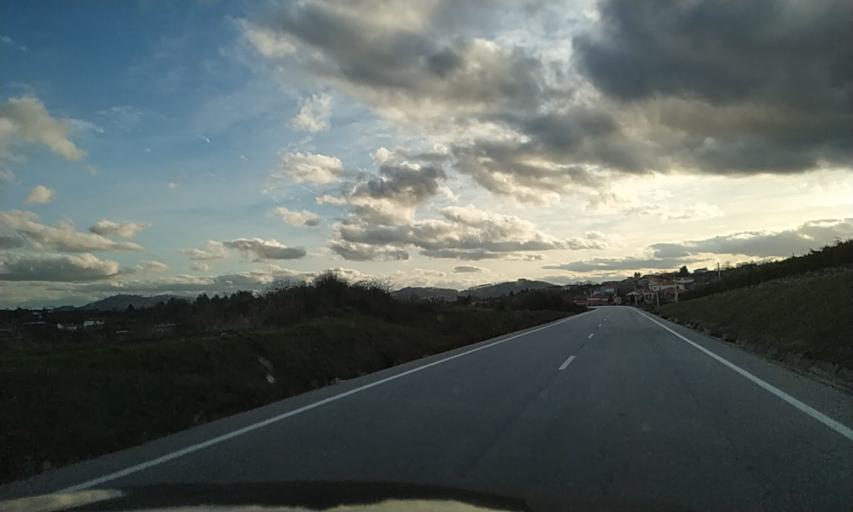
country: PT
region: Braganca
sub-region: Carrazeda de Ansiaes
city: Carrazeda de Anciaes
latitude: 41.2388
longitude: -7.3218
